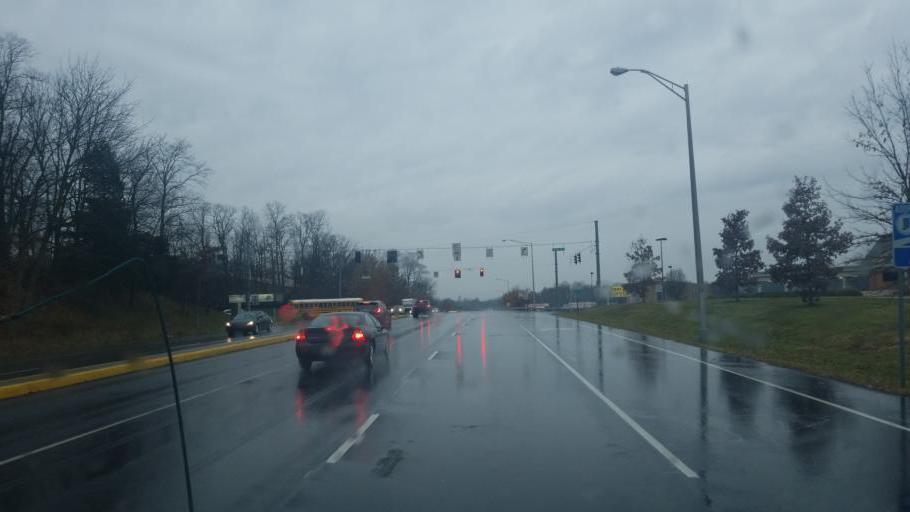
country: US
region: Indiana
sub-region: Bartholomew County
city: Columbus
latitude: 39.2000
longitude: -85.9676
